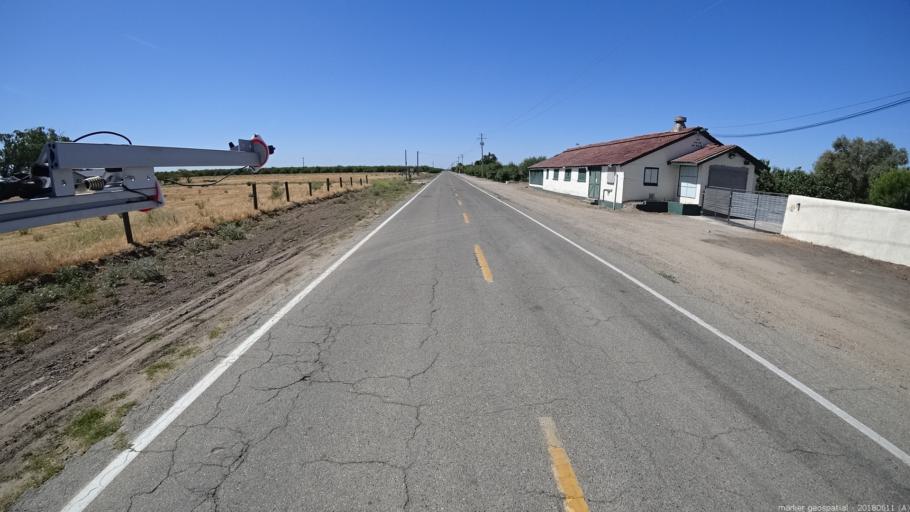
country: US
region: California
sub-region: Madera County
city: Fairmead
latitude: 36.9945
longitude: -120.2023
